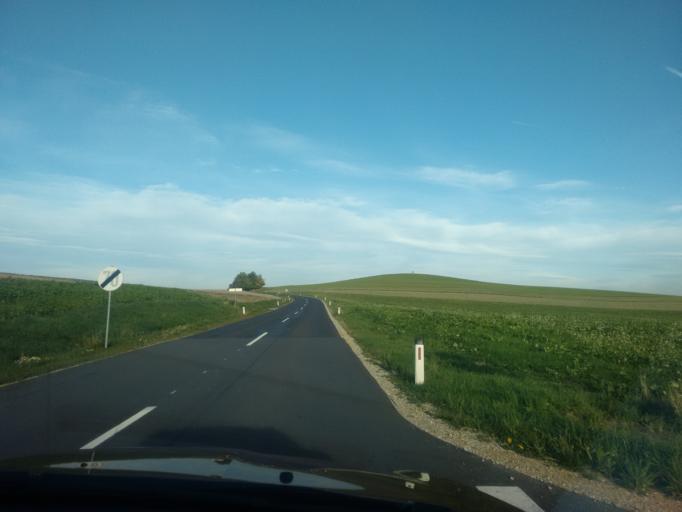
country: AT
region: Upper Austria
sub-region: Politischer Bezirk Vocklabruck
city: Wolfsegg am Hausruck
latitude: 48.1214
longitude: 13.6966
